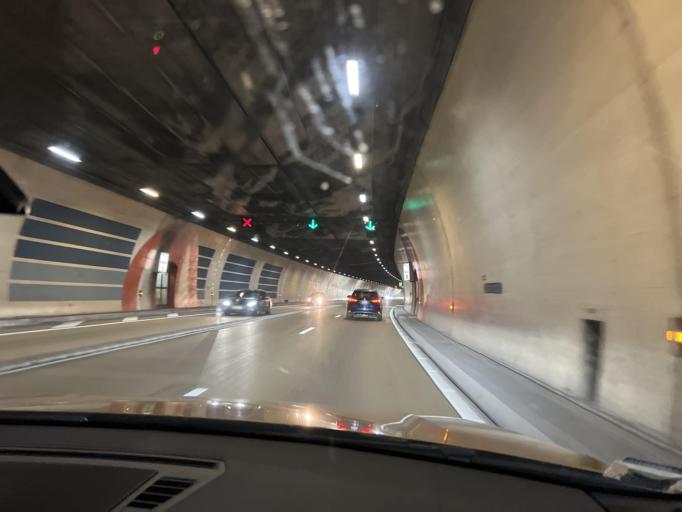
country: FR
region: Provence-Alpes-Cote d'Azur
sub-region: Departement des Alpes-Maritimes
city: La Turbie
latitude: 43.7359
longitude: 7.3855
